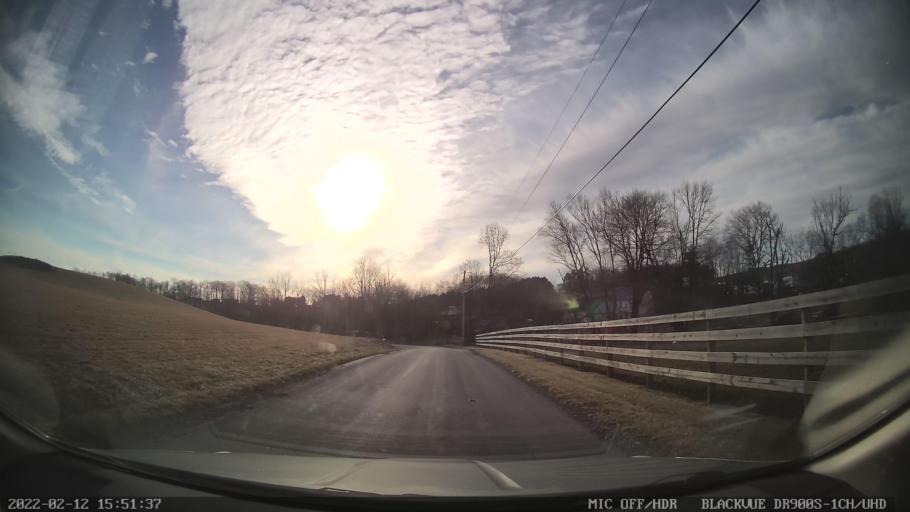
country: US
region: Pennsylvania
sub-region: Berks County
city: Kutztown
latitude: 40.5748
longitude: -75.7656
